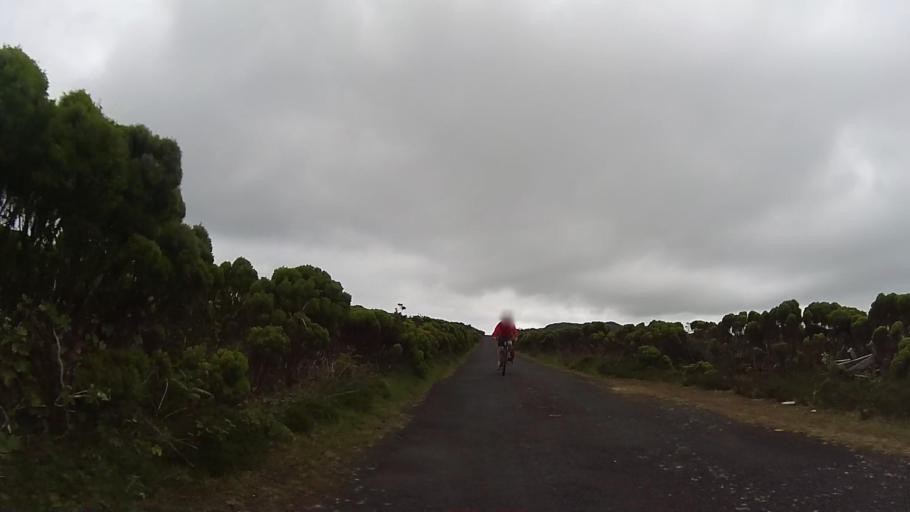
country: PT
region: Azores
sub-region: Sao Roque do Pico
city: Sao Roque do Pico
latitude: 38.4651
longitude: -28.2884
